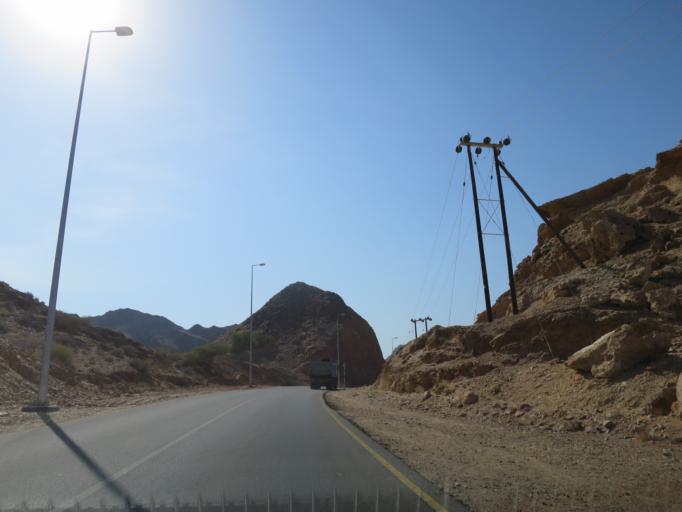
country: OM
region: Muhafazat Masqat
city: Muscat
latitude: 23.5163
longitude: 58.7126
